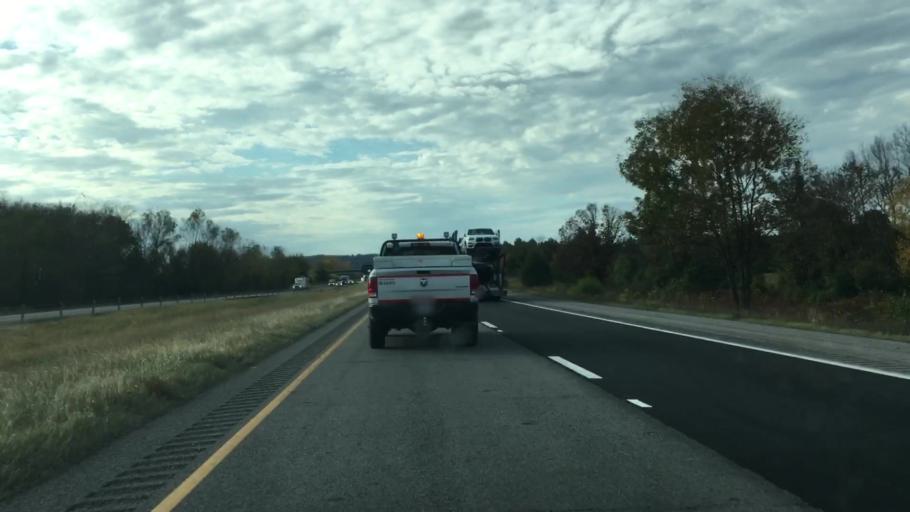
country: US
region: Arkansas
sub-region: Pope County
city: Atkins
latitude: 35.2504
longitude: -92.8845
